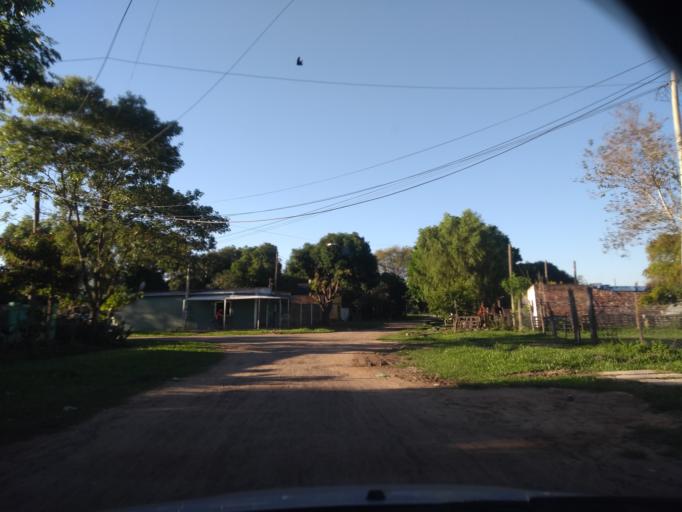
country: AR
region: Chaco
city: Barranqueras
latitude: -27.4790
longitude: -58.9250
